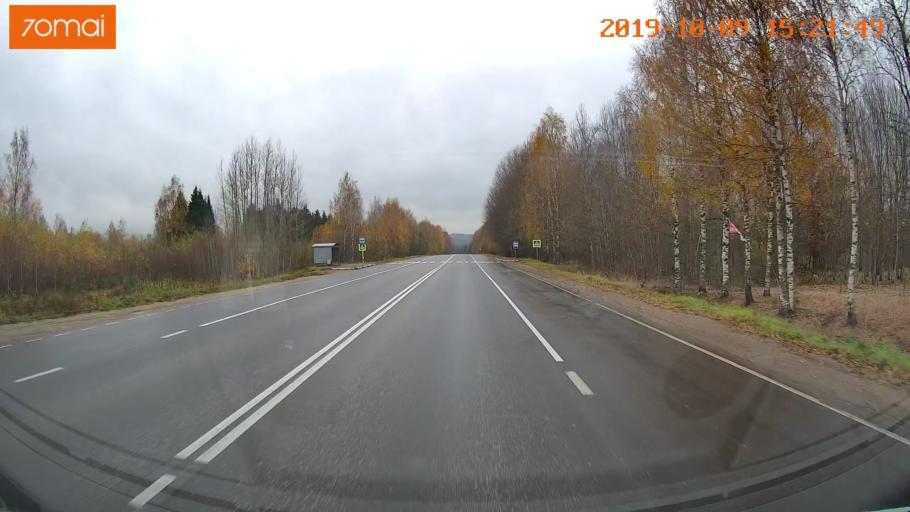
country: RU
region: Kostroma
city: Susanino
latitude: 58.0509
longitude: 41.5106
